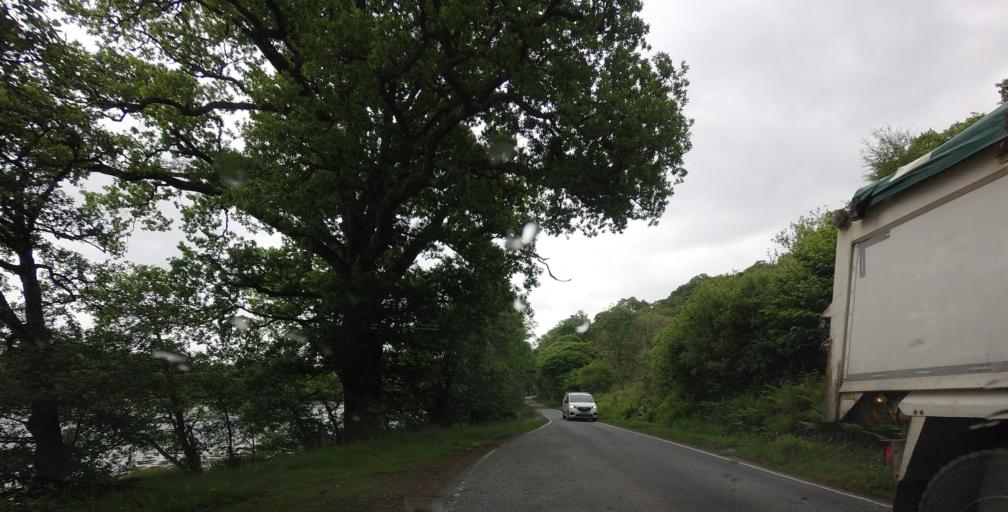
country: GB
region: Scotland
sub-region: Highland
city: Fort William
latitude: 56.8426
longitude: -5.1668
